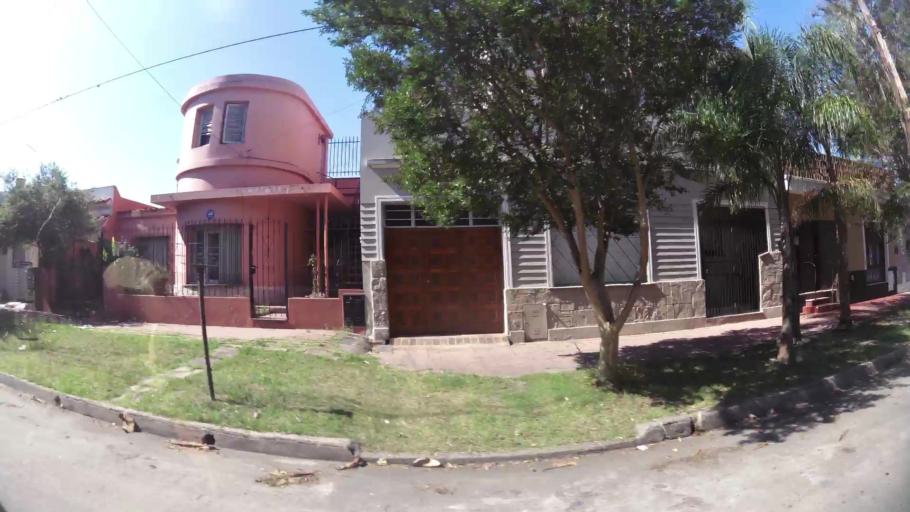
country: AR
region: Cordoba
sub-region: Departamento de Capital
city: Cordoba
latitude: -31.4181
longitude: -64.1616
